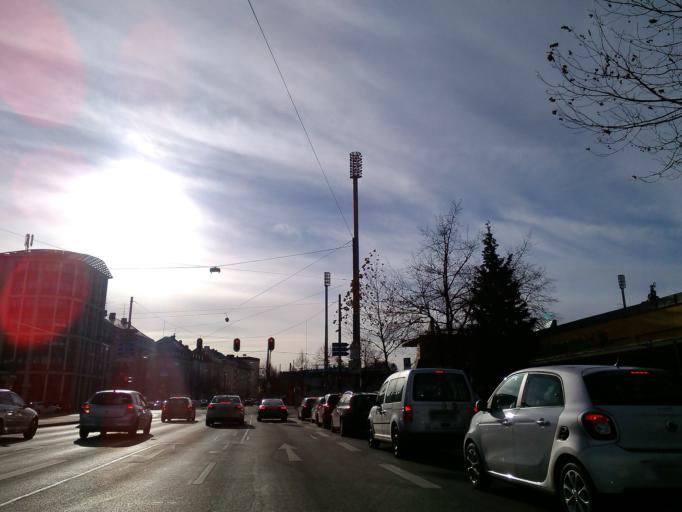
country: DE
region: Bavaria
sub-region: Upper Bavaria
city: Munich
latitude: 48.1123
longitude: 11.5761
